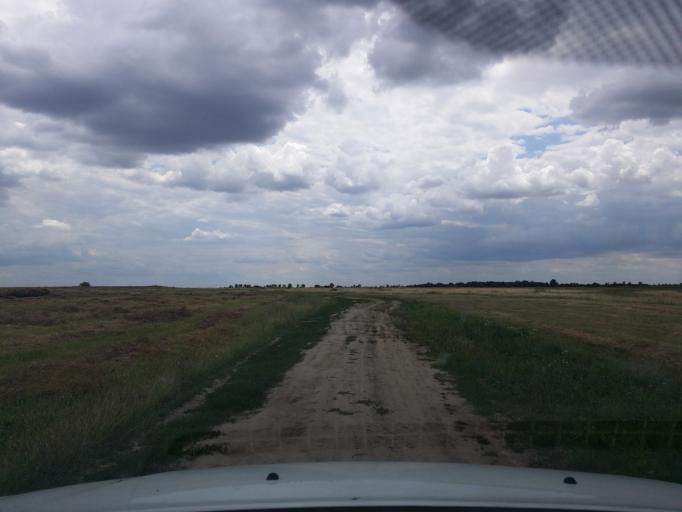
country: HU
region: Hajdu-Bihar
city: Egyek
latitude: 47.5655
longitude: 20.9443
